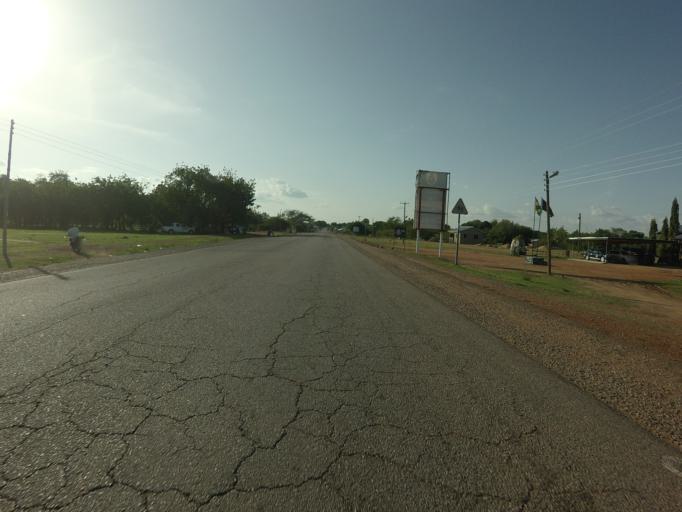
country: GH
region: Upper East
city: Navrongo
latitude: 10.9578
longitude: -1.0980
